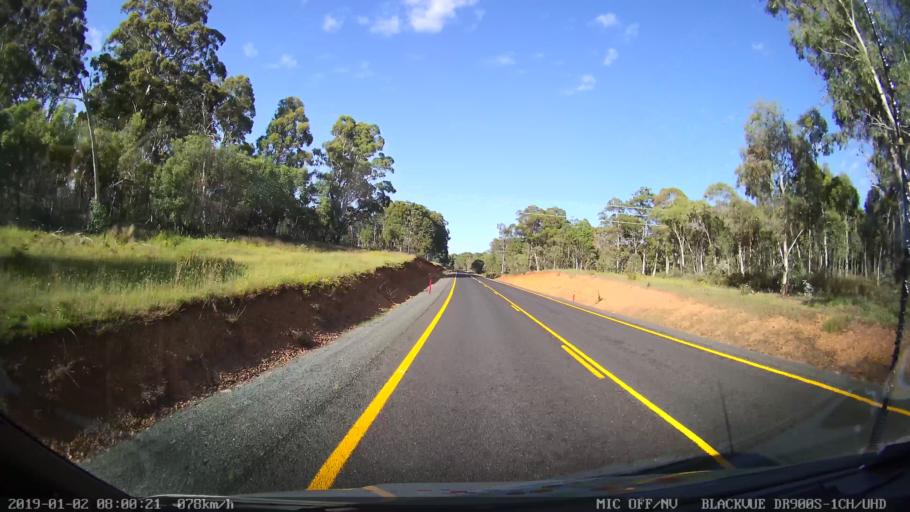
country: AU
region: New South Wales
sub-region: Tumut Shire
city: Tumut
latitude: -35.6441
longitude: 148.4466
